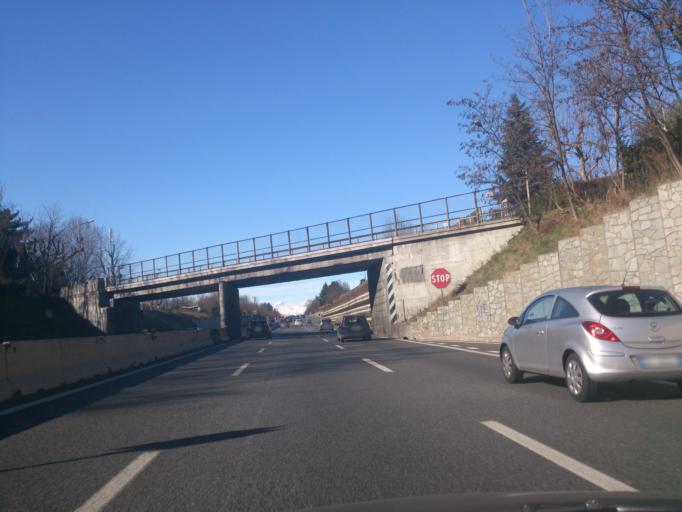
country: IT
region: Lombardy
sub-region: Provincia di Varese
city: Olgiate Olona
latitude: 45.6283
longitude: 8.8853
